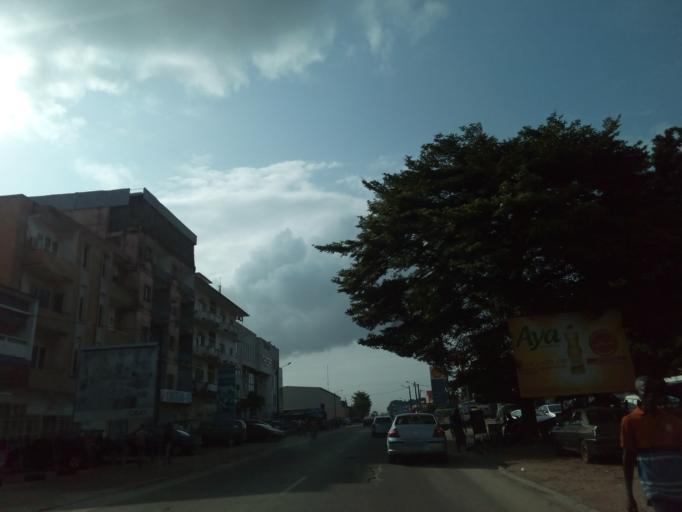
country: CI
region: Lagunes
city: Abidjan
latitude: 5.2946
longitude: -4.0024
